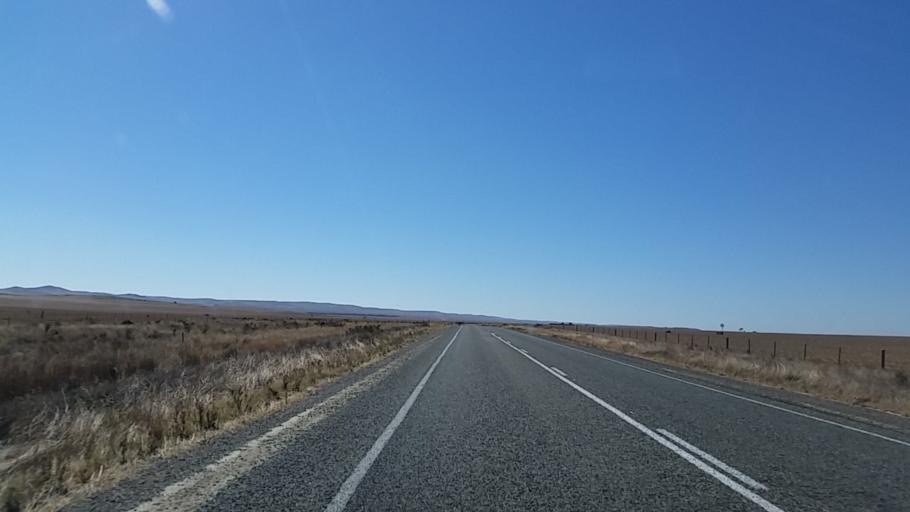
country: AU
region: South Australia
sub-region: Northern Areas
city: Jamestown
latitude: -33.2788
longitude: 138.8687
